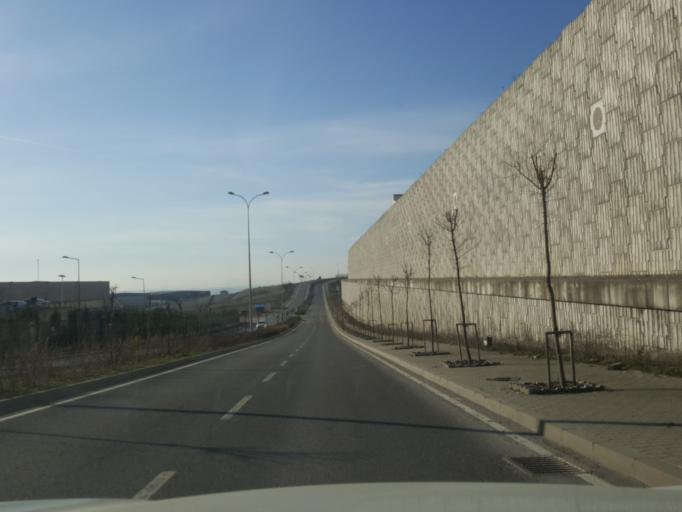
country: TR
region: Kocaeli
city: Tavsanli
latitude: 40.8319
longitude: 29.5559
